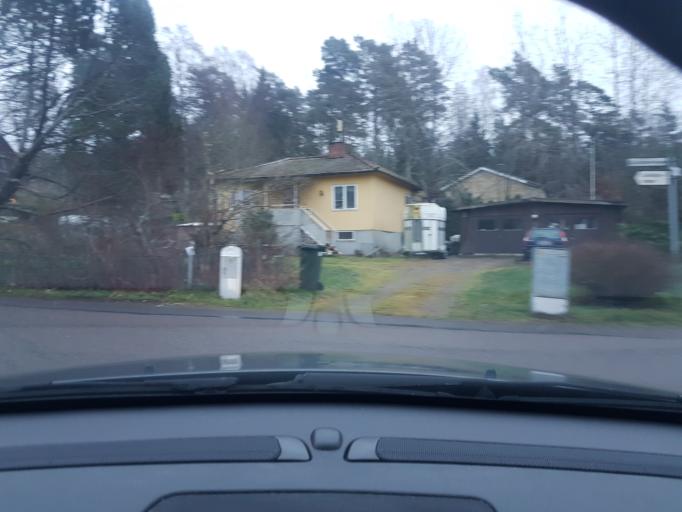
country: SE
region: Vaestra Goetaland
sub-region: Ale Kommun
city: Alvangen
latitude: 57.9527
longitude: 12.1313
